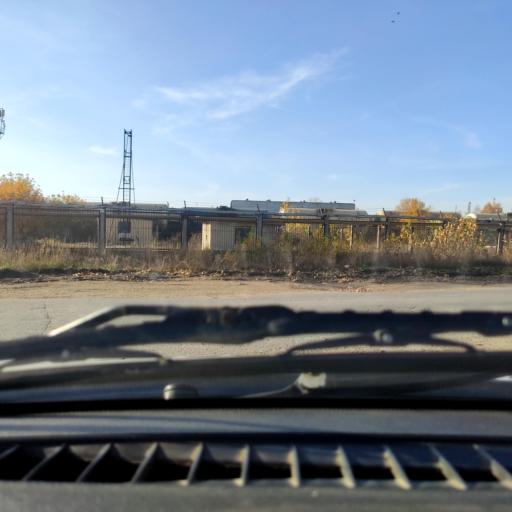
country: RU
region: Samara
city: Zhigulevsk
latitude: 53.4720
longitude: 49.5011
